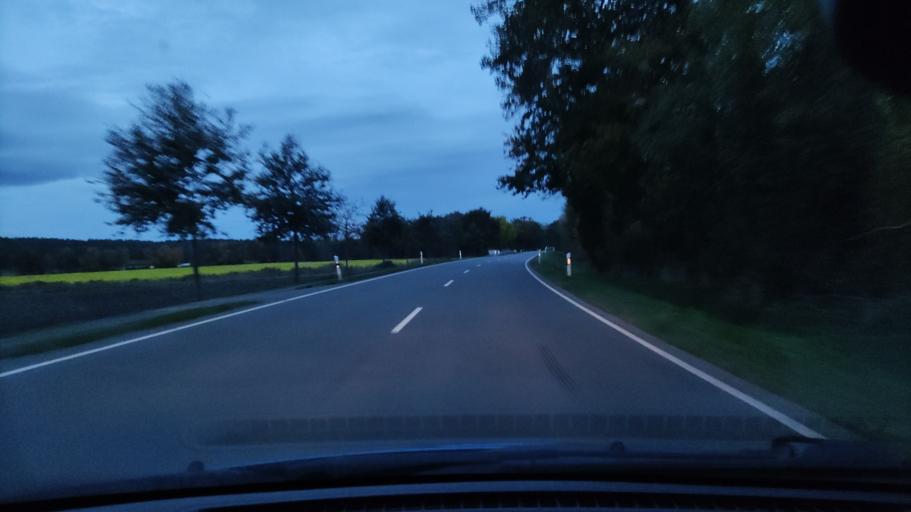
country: DE
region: Lower Saxony
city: Woltersdorf
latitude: 52.9630
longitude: 11.2540
